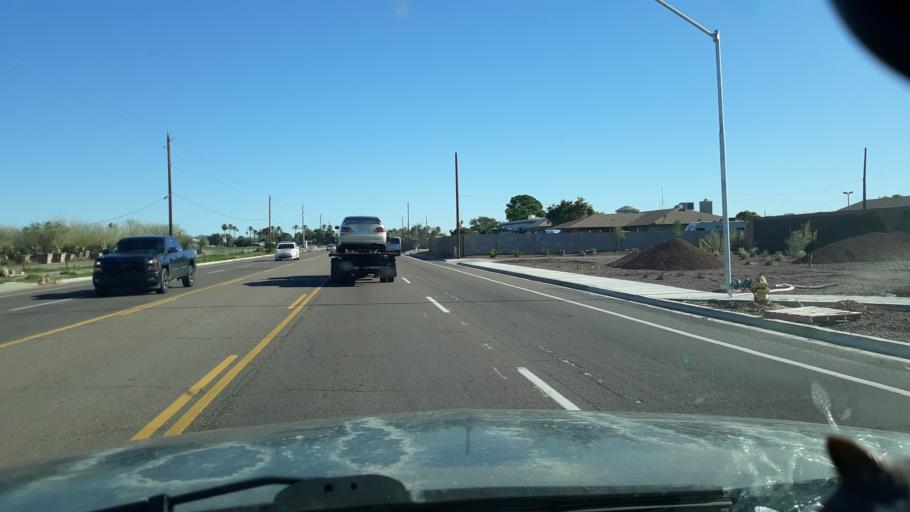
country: US
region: Arizona
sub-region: Maricopa County
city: Peoria
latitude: 33.5520
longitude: -112.2353
